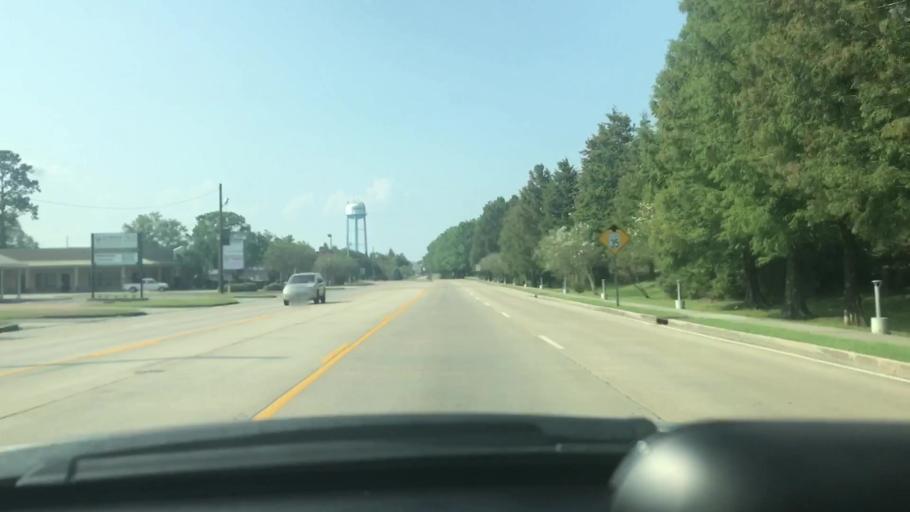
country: US
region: Louisiana
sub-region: Tangipahoa Parish
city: Hammond
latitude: 30.4957
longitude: -90.4588
